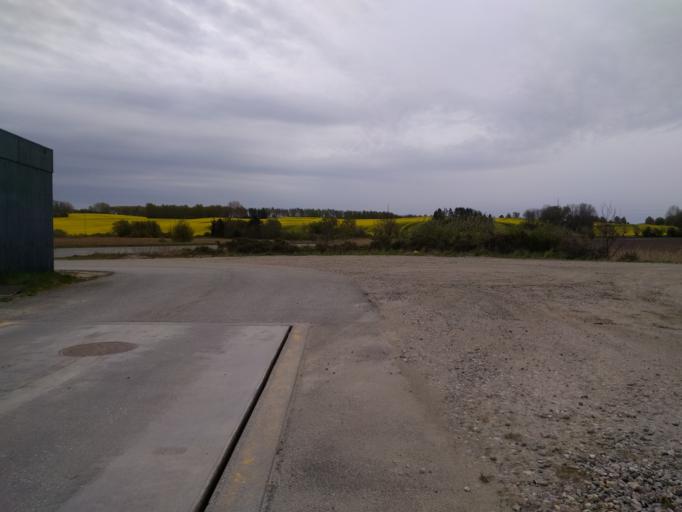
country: DK
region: South Denmark
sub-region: Kerteminde Kommune
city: Munkebo
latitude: 55.4711
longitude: 10.5512
